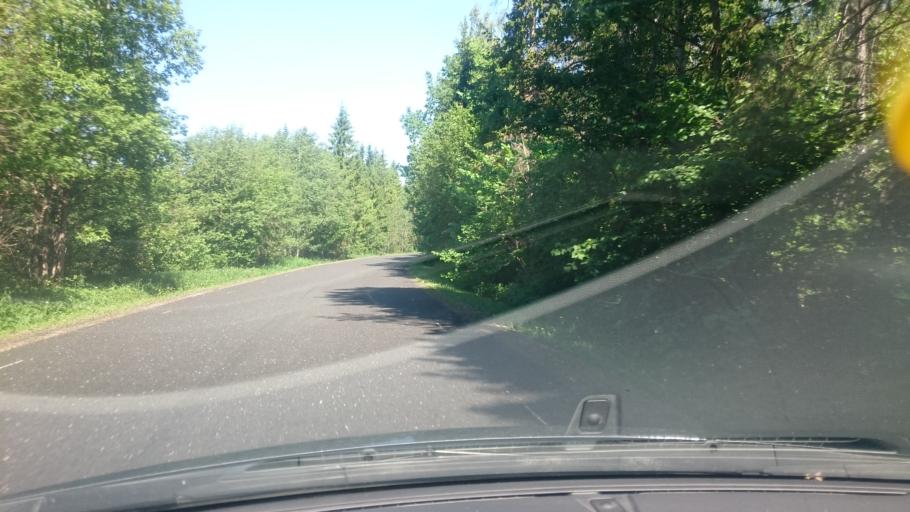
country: EE
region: Harju
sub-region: Rae vald
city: Vaida
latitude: 59.2107
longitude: 24.9505
